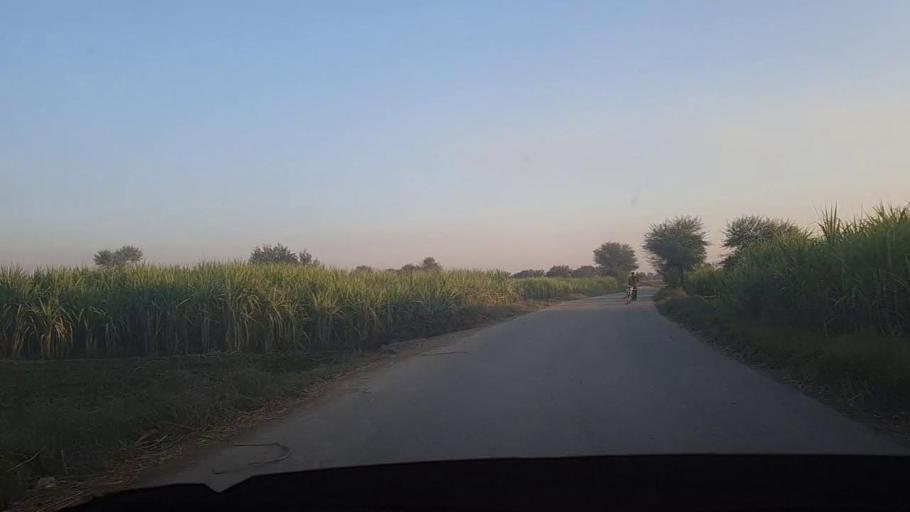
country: PK
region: Sindh
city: Sobhadero
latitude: 27.3514
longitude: 68.3749
